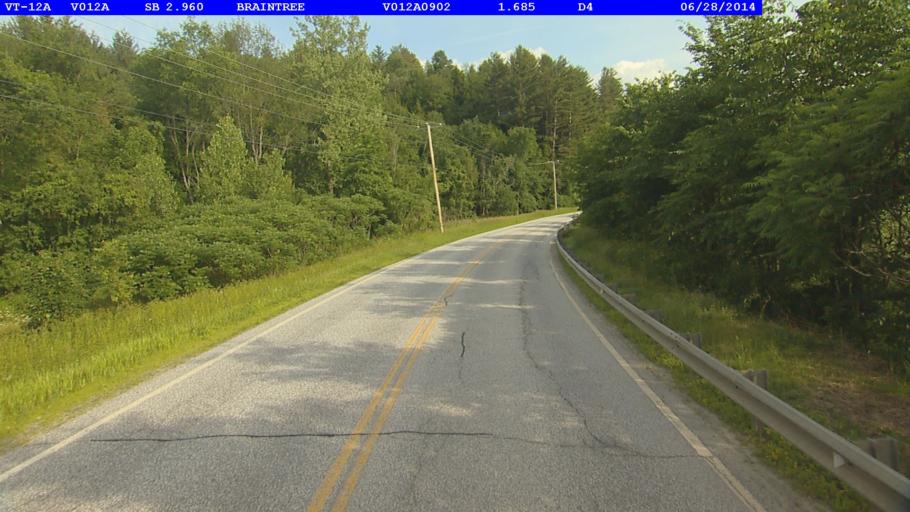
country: US
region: Vermont
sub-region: Orange County
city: Randolph
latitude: 43.9455
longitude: -72.7087
